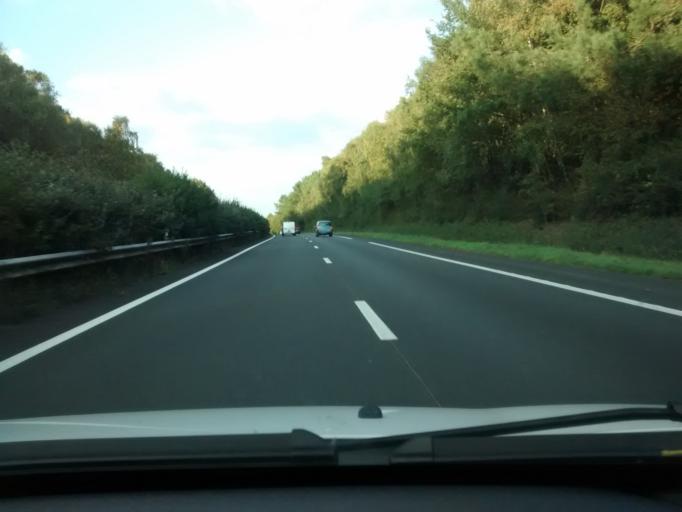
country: FR
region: Pays de la Loire
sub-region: Departement de la Loire-Atlantique
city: Nozay
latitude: 47.5815
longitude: -1.6281
